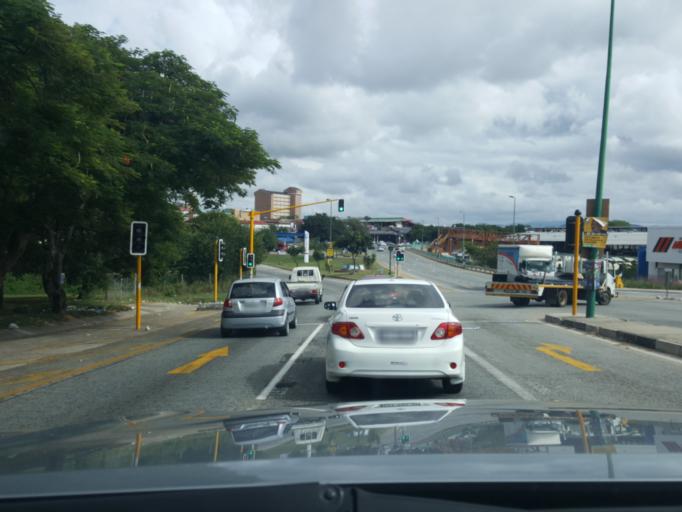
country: ZA
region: Mpumalanga
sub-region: Ehlanzeni District
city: Nelspruit
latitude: -25.4701
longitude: 30.9852
